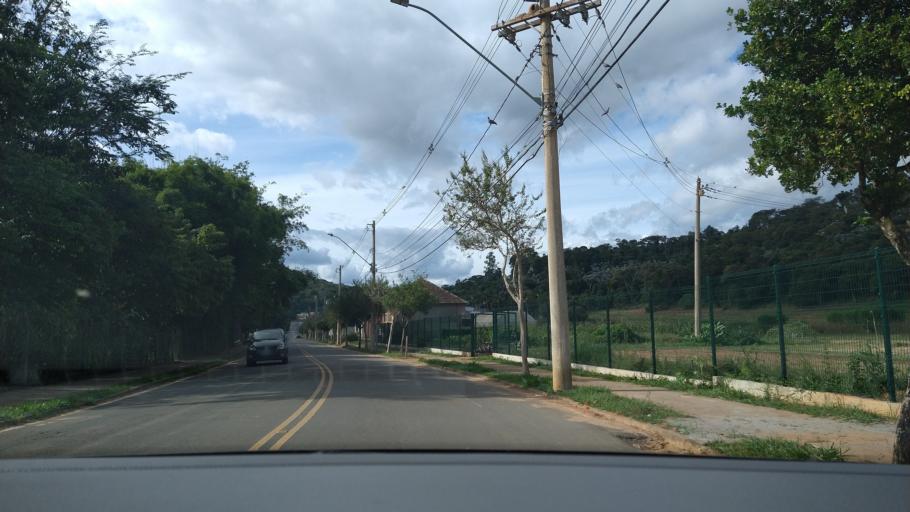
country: BR
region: Minas Gerais
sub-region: Vicosa
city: Vicosa
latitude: -20.7690
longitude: -42.8711
